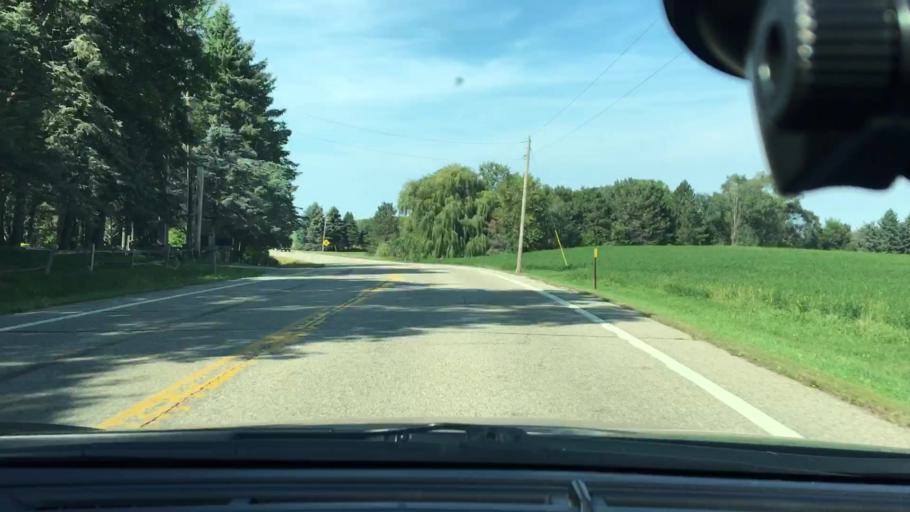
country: US
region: Minnesota
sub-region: Hennepin County
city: Corcoran
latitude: 45.1200
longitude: -93.6013
